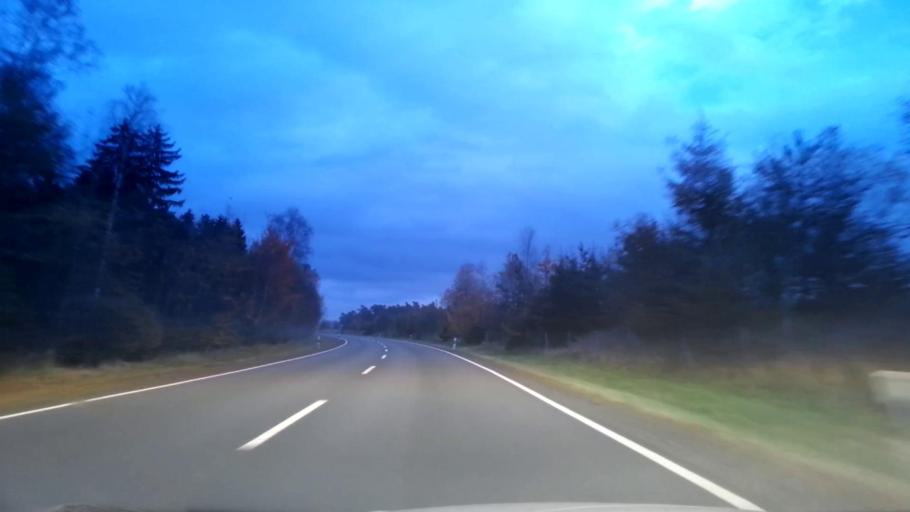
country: DE
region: Bavaria
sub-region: Upper Palatinate
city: Pechbrunn
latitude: 49.9543
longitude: 12.1960
